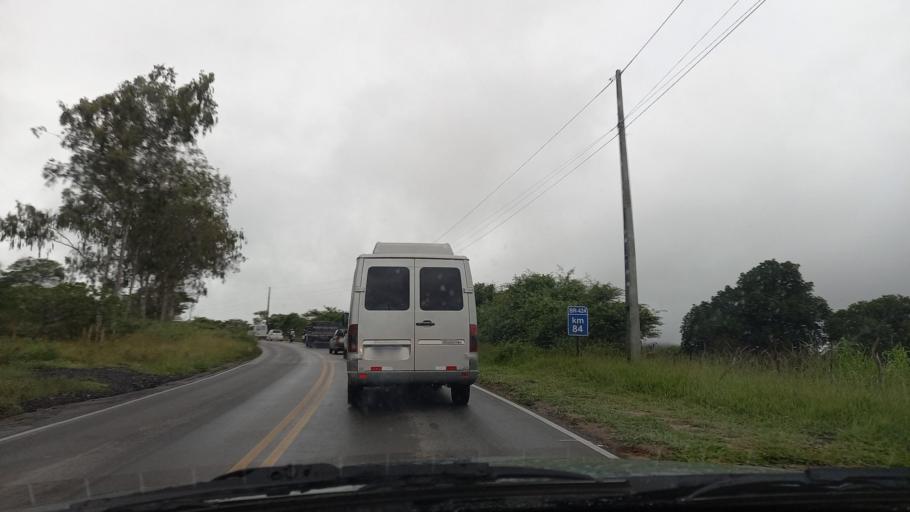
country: BR
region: Pernambuco
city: Garanhuns
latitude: -8.8526
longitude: -36.5151
